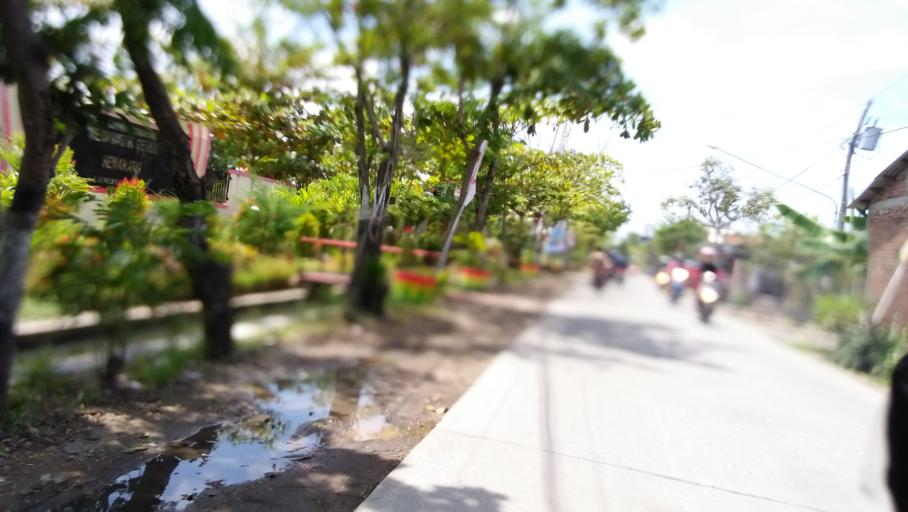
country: ID
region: Central Java
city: Semarang
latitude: -6.9650
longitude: 110.4775
